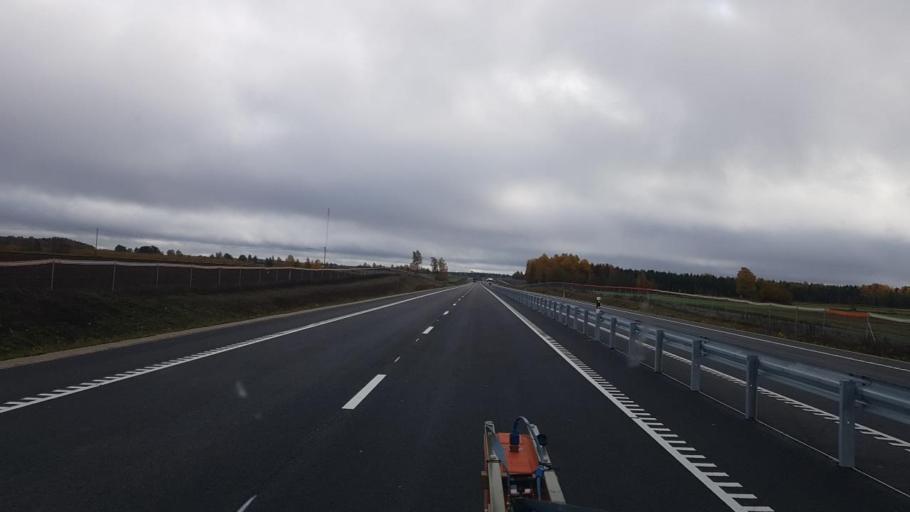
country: EE
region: Jaervamaa
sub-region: Paide linn
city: Paide
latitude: 59.0033
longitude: 25.5716
